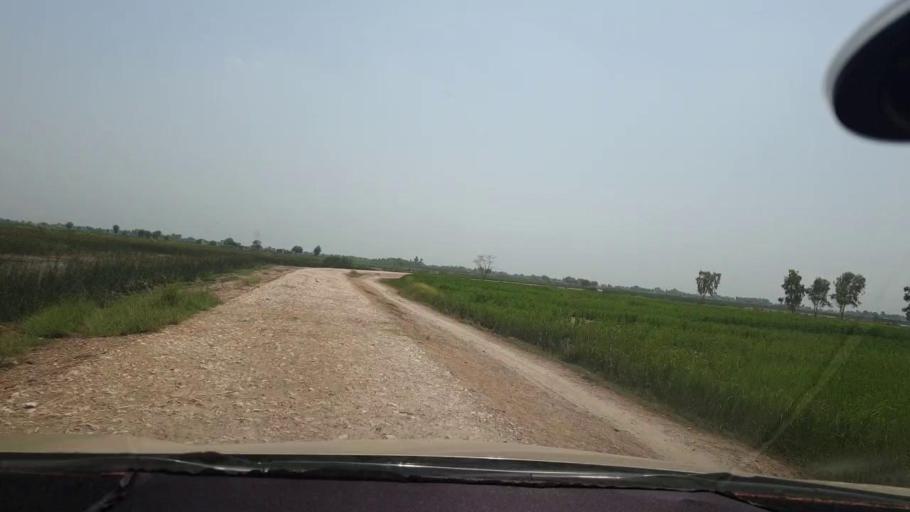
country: PK
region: Sindh
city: Kambar
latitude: 27.6512
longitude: 67.9322
